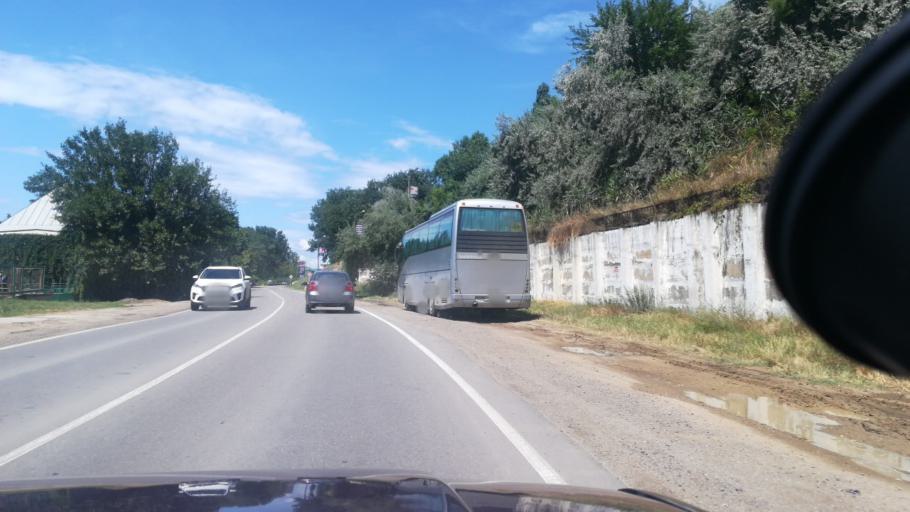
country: RU
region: Krasnodarskiy
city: Vityazevo
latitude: 44.9753
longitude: 37.2759
